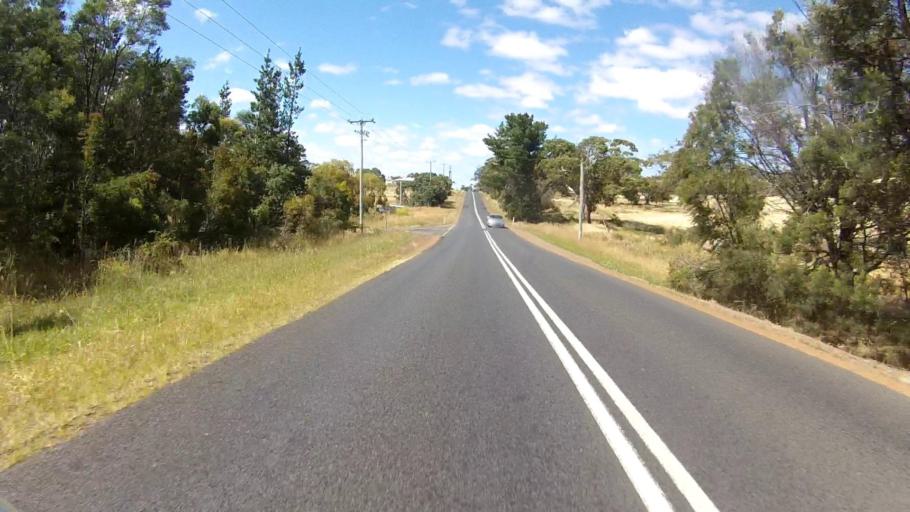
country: AU
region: Tasmania
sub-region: Sorell
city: Sorell
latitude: -42.6148
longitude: 147.4283
